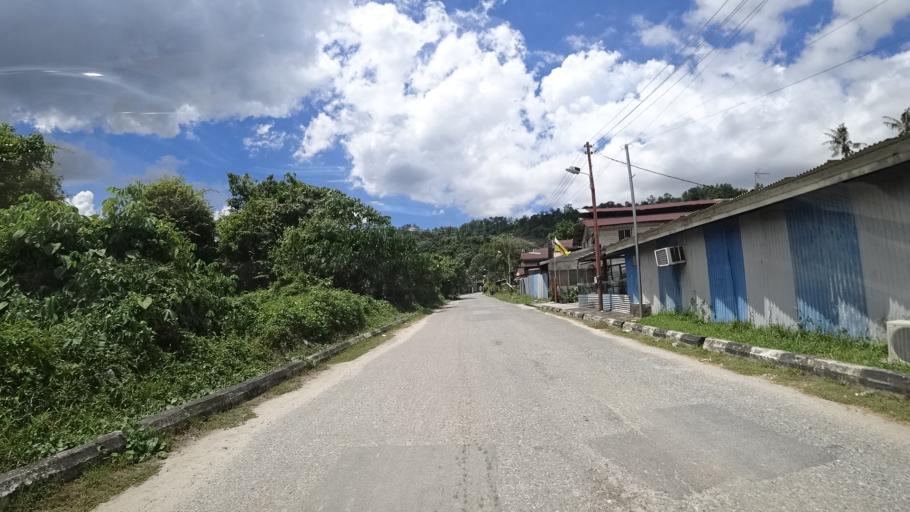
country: BN
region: Brunei and Muara
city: Bandar Seri Begawan
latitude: 4.8550
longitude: 114.8934
